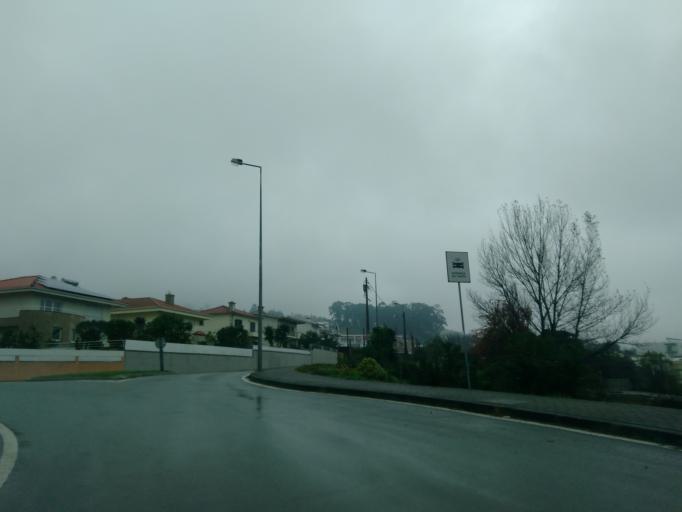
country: PT
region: Braga
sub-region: Braga
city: Adaufe
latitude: 41.5686
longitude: -8.3798
